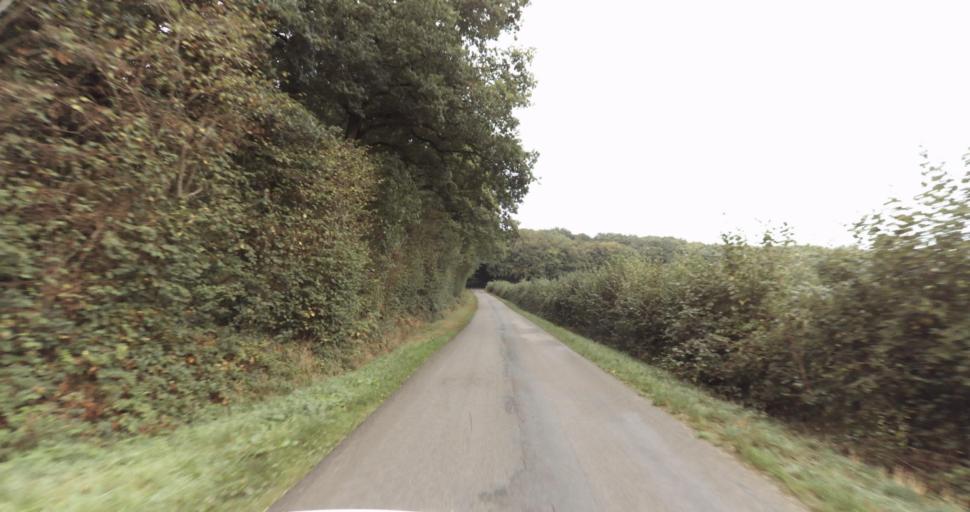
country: FR
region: Lower Normandy
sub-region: Departement de l'Orne
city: Trun
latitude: 48.8862
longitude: 0.0930
